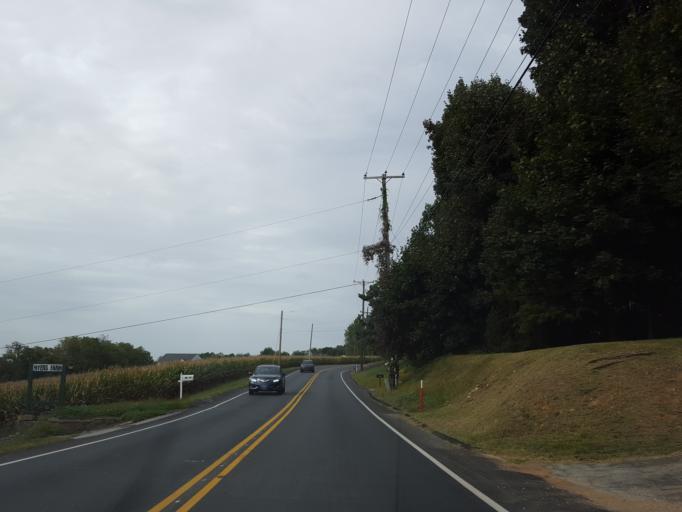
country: US
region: Pennsylvania
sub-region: York County
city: Spry
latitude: 39.9101
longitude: -76.6865
